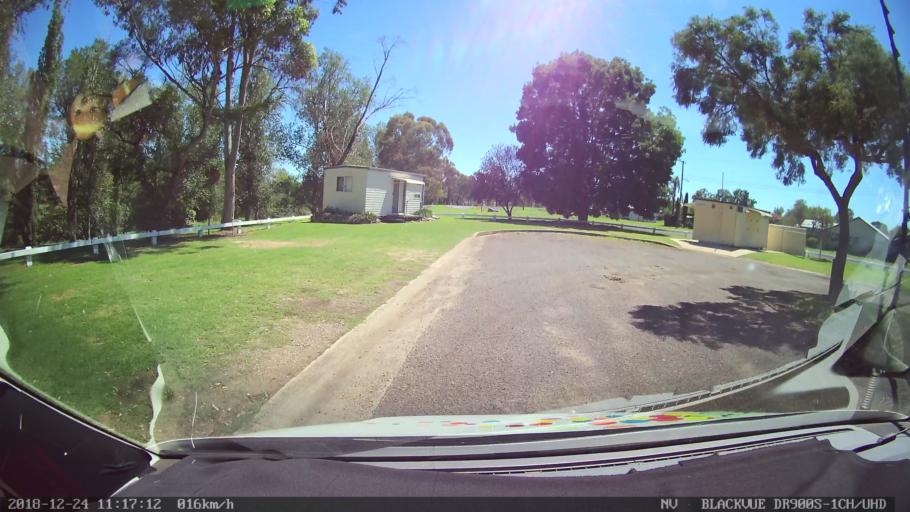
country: AU
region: New South Wales
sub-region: Upper Hunter Shire
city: Merriwa
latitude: -32.1386
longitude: 150.3503
